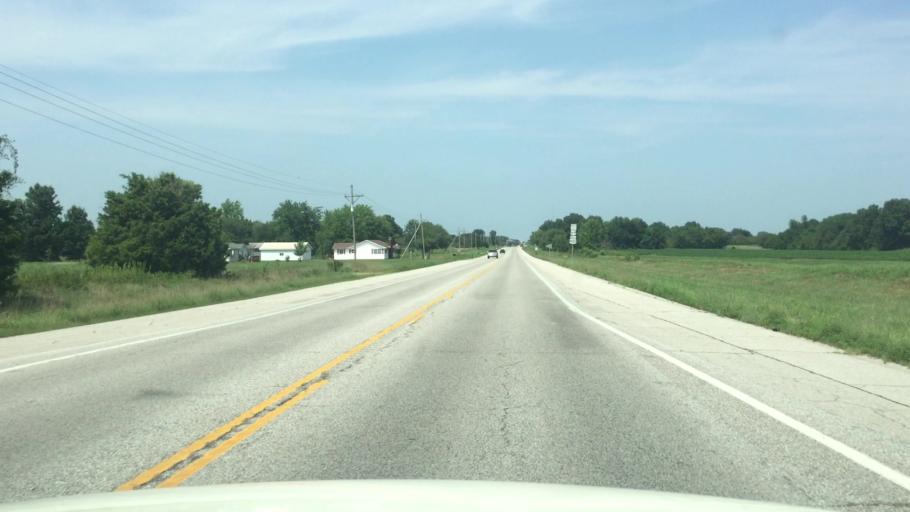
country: US
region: Kansas
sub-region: Cherokee County
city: Galena
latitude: 37.1058
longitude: -94.7043
